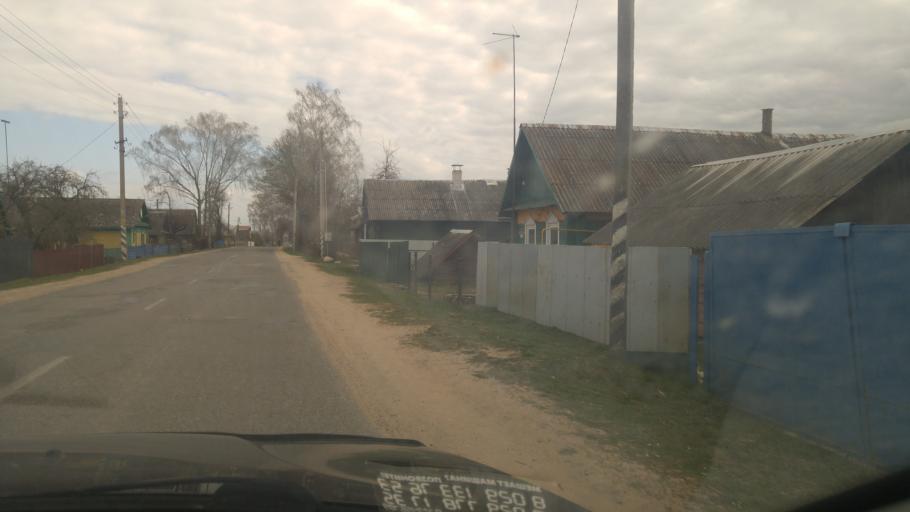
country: BY
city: Michanovichi
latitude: 53.6621
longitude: 27.7711
